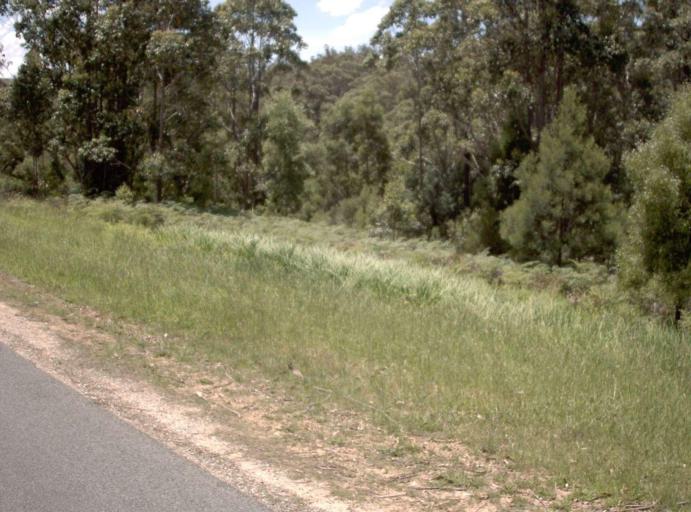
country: AU
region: New South Wales
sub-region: Bombala
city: Bombala
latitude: -37.5437
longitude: 148.9371
